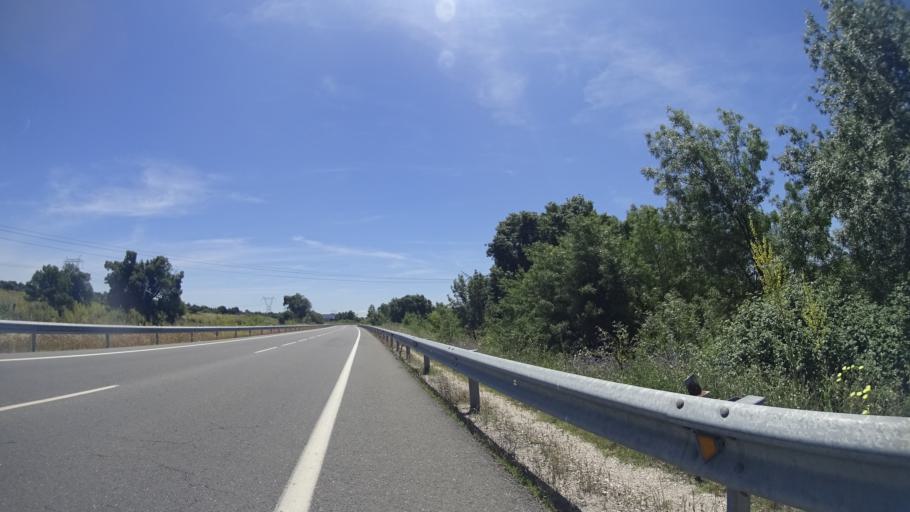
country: ES
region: Madrid
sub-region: Provincia de Madrid
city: Galapagar
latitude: 40.5883
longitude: -4.0056
